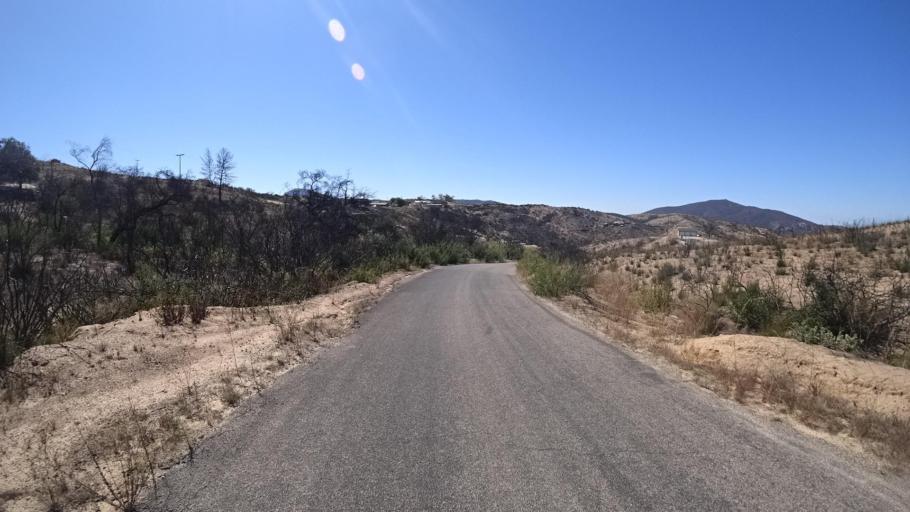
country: US
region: California
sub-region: San Diego County
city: Alpine
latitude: 32.7722
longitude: -116.7646
